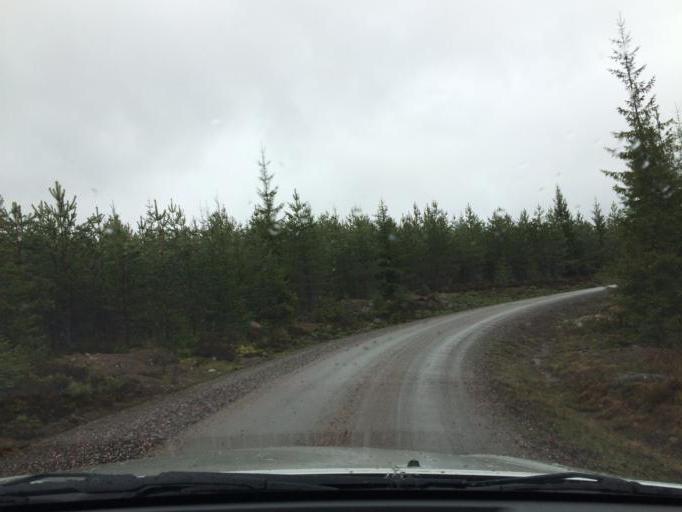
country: SE
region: OErebro
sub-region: Hallefors Kommun
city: Haellefors
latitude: 60.0263
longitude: 14.5575
